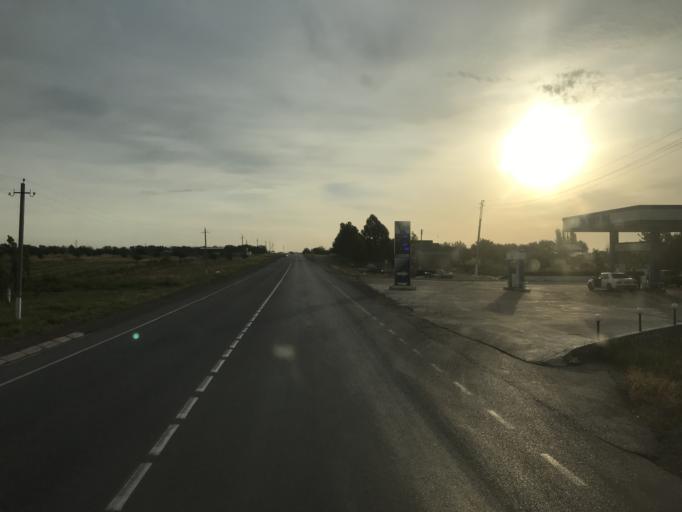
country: KZ
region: Ongtustik Qazaqstan
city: Saryaghash
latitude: 41.4338
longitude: 69.1140
